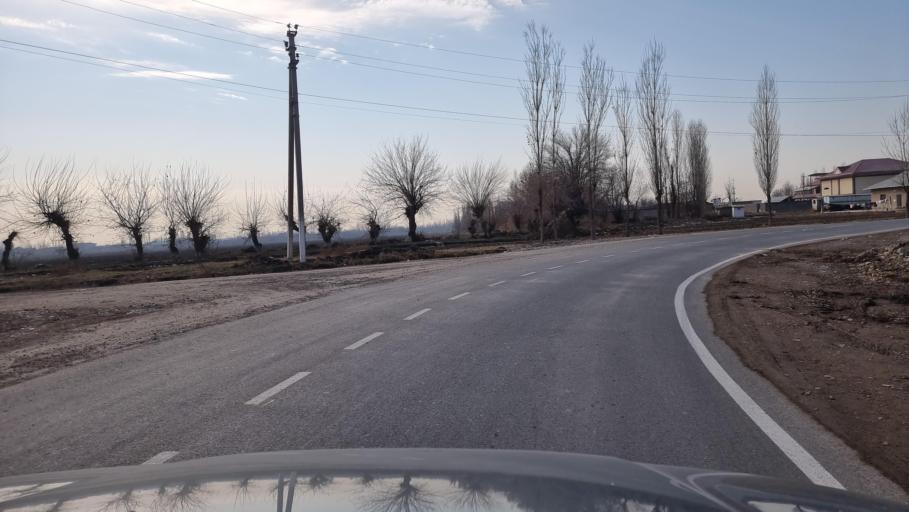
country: UZ
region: Toshkent
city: Tuytepa
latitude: 41.0905
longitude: 69.3678
